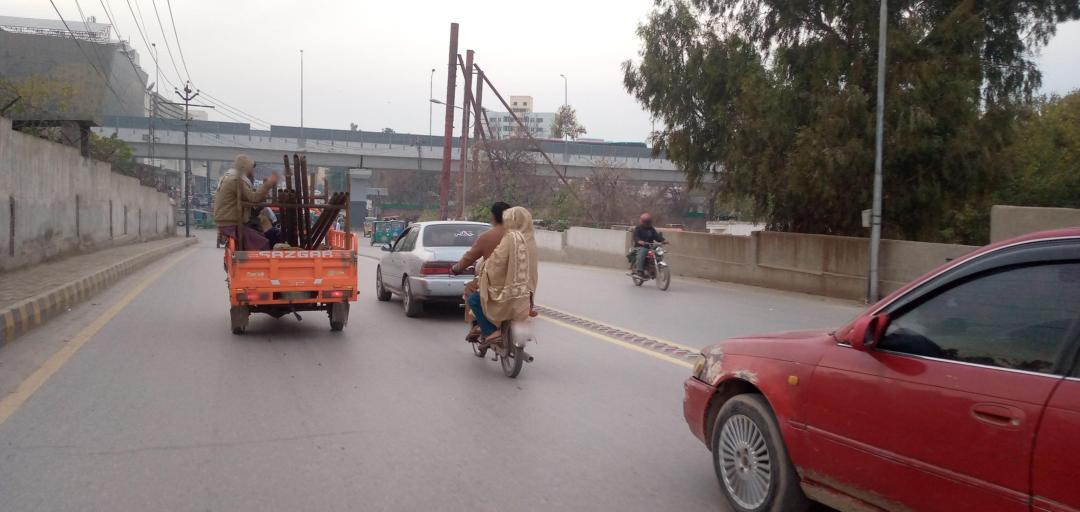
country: PK
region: Khyber Pakhtunkhwa
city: Peshawar
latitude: 33.9998
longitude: 71.5472
